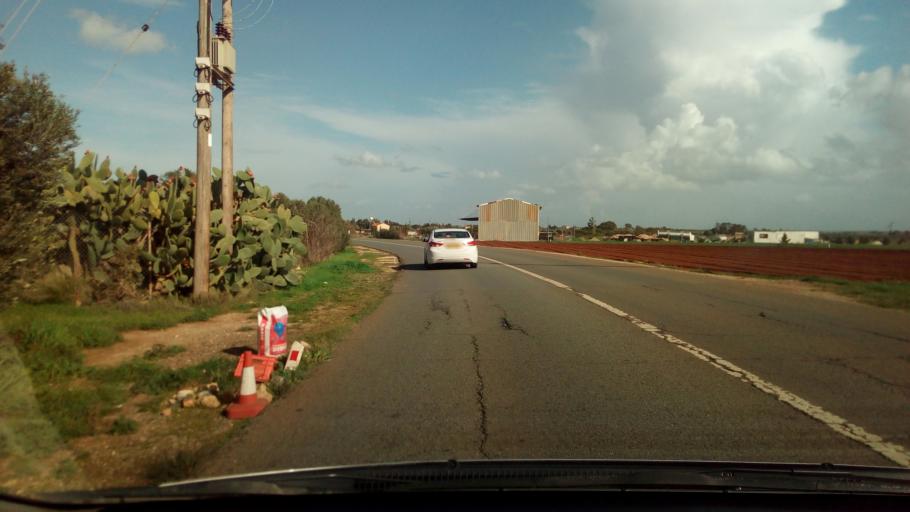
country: CY
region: Ammochostos
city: Achna
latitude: 35.0479
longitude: 33.7907
